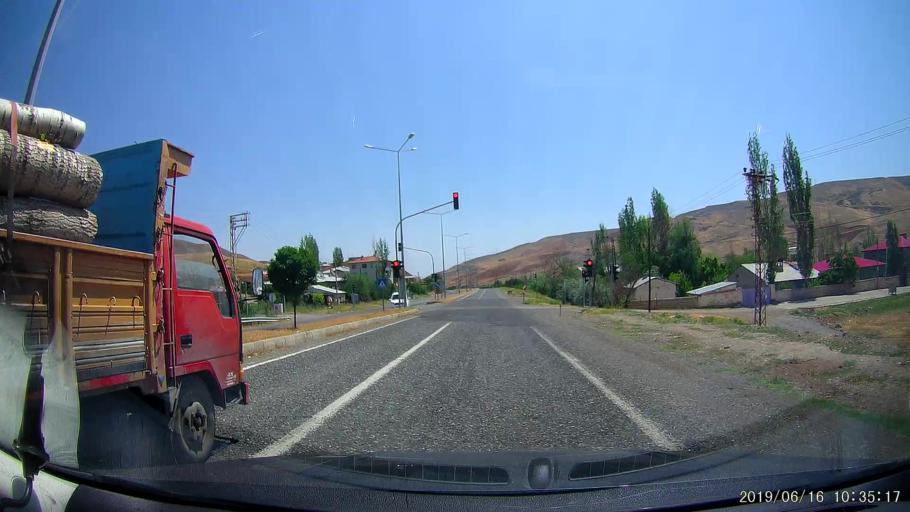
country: TR
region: Igdir
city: Tuzluca
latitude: 40.0355
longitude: 43.6706
